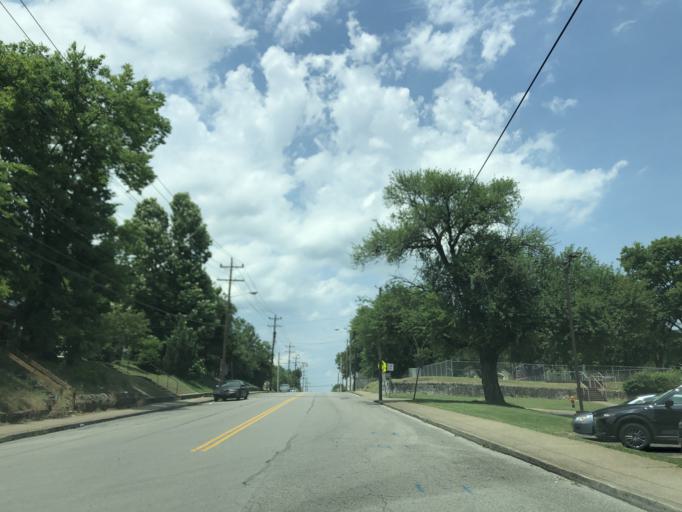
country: US
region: Tennessee
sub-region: Davidson County
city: Nashville
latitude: 36.1802
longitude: -86.7551
